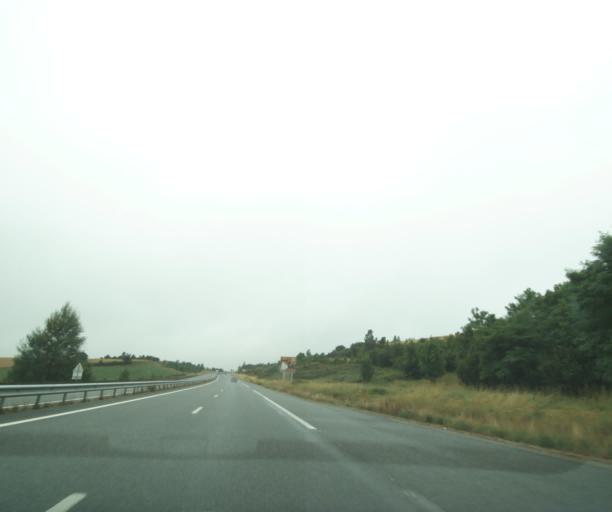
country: FR
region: Midi-Pyrenees
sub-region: Departement de l'Aveyron
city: Naucelle
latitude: 44.1235
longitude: 2.3096
